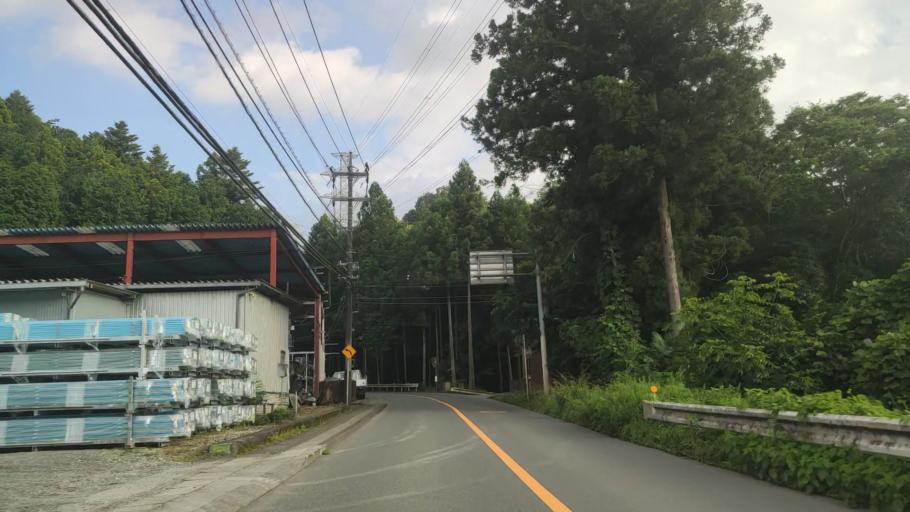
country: JP
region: Saitama
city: Hanno
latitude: 35.8306
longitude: 139.2701
